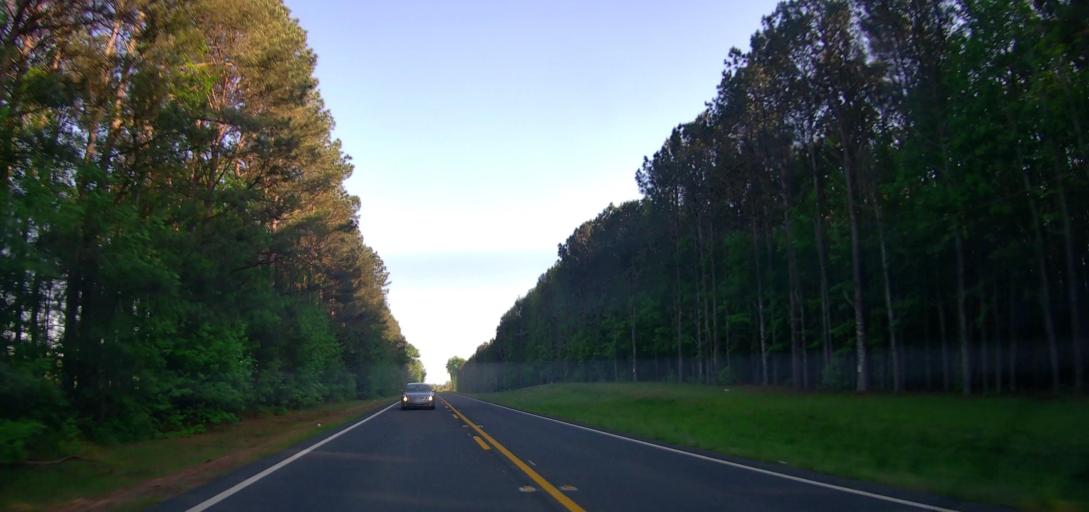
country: US
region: Georgia
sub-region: Jasper County
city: Monticello
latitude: 33.4821
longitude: -83.6460
